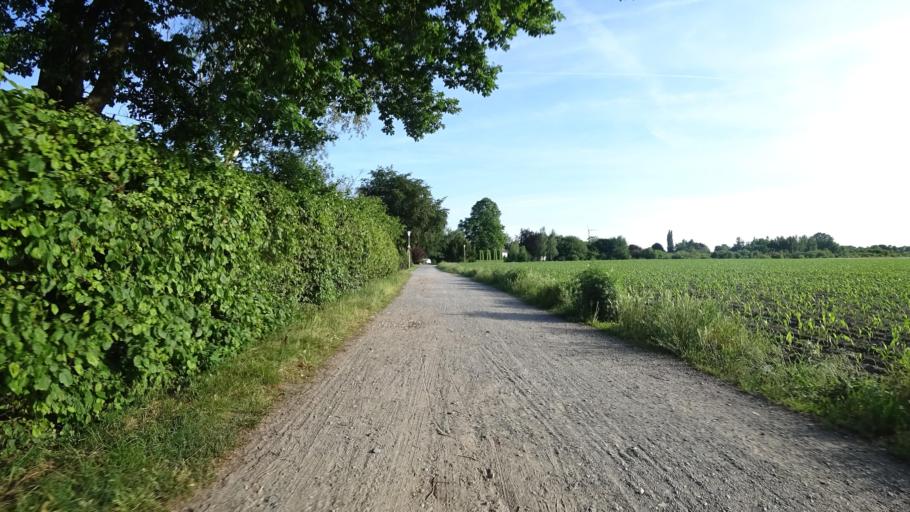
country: DE
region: North Rhine-Westphalia
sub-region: Regierungsbezirk Detmold
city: Guetersloh
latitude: 51.8922
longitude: 8.4219
